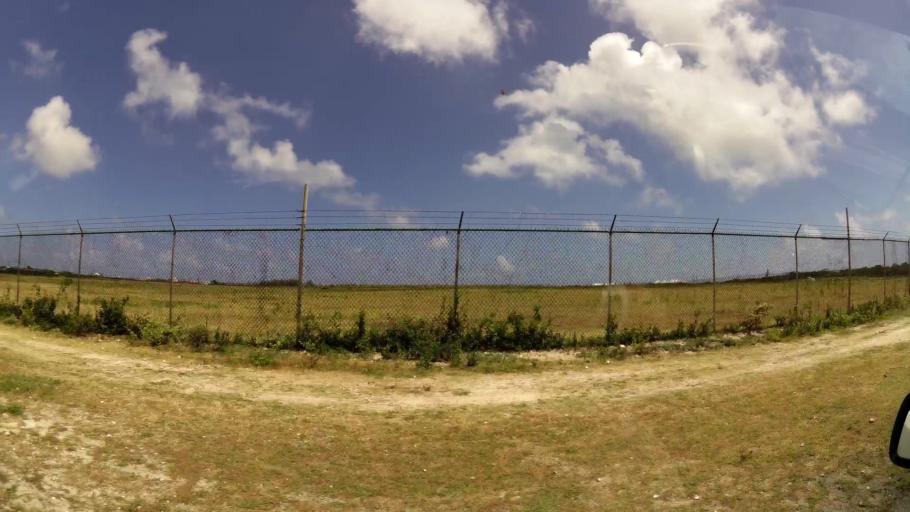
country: TC
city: Cockburn Town
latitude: 21.4458
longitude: -71.1529
